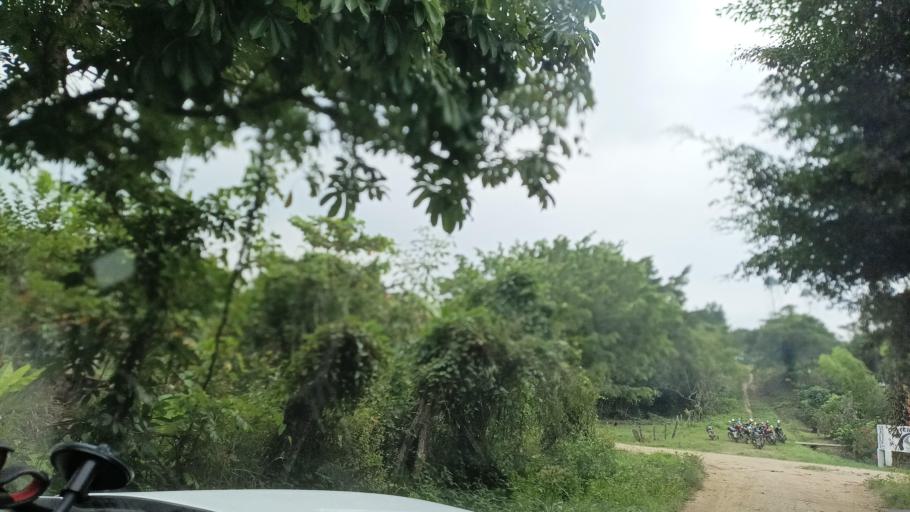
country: MX
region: Veracruz
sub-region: Moloacan
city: Cuichapa
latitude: 17.5787
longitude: -94.2299
